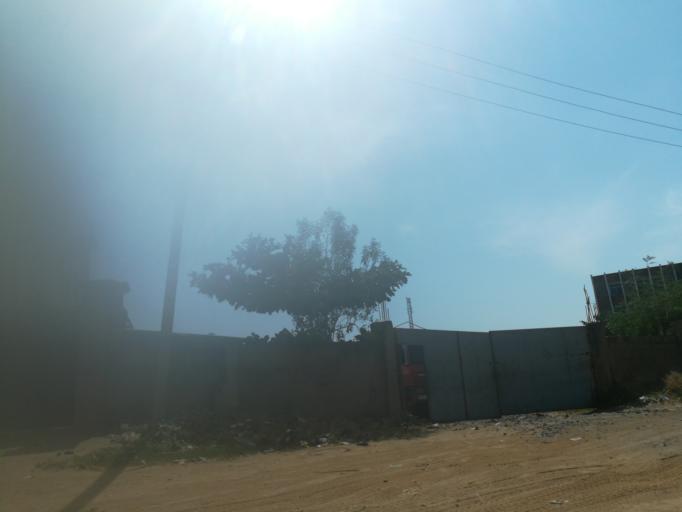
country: NG
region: Kano
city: Kano
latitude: 12.0294
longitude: 8.5143
